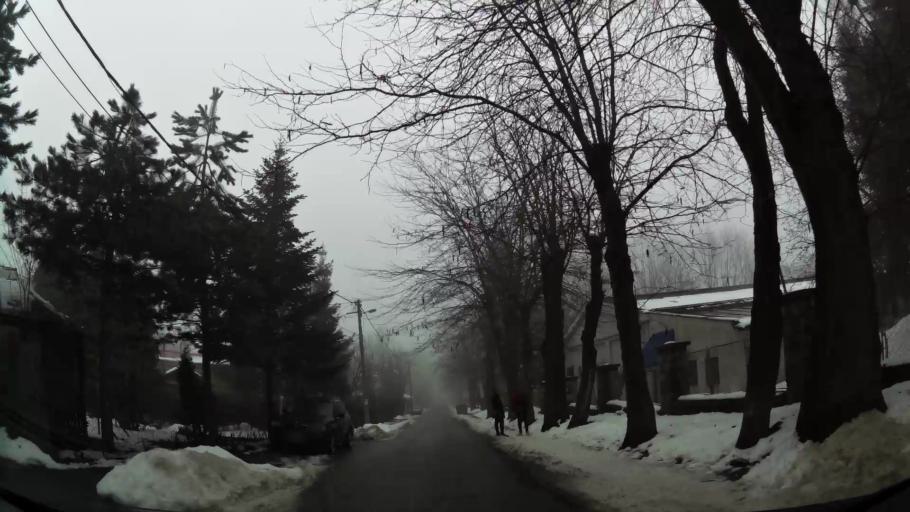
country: RS
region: Central Serbia
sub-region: Belgrade
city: Savski Venac
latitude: 44.7719
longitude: 20.4595
